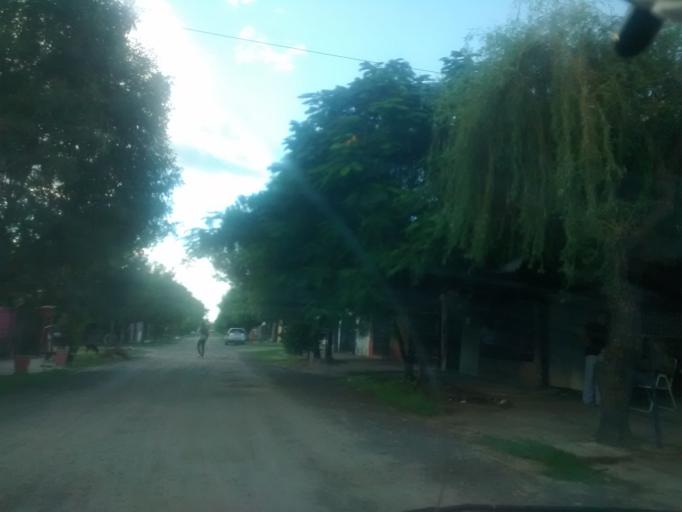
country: AR
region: Chaco
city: Fontana
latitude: -27.4510
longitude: -59.0224
